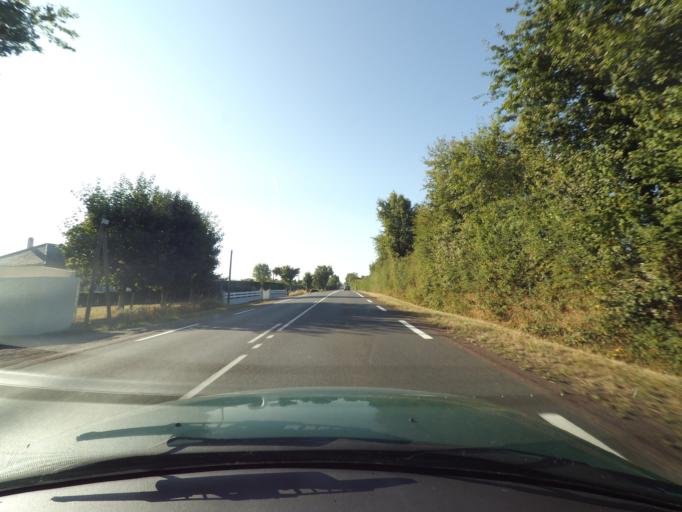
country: FR
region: Poitou-Charentes
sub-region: Departement des Deux-Sevres
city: Viennay
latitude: 46.6867
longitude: -0.2692
